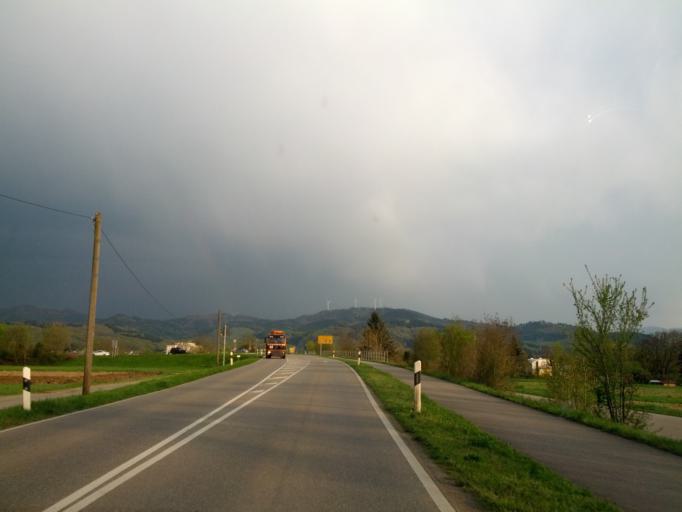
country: DE
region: Baden-Wuerttemberg
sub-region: Freiburg Region
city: Gundelfingen
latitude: 48.0521
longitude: 7.8567
